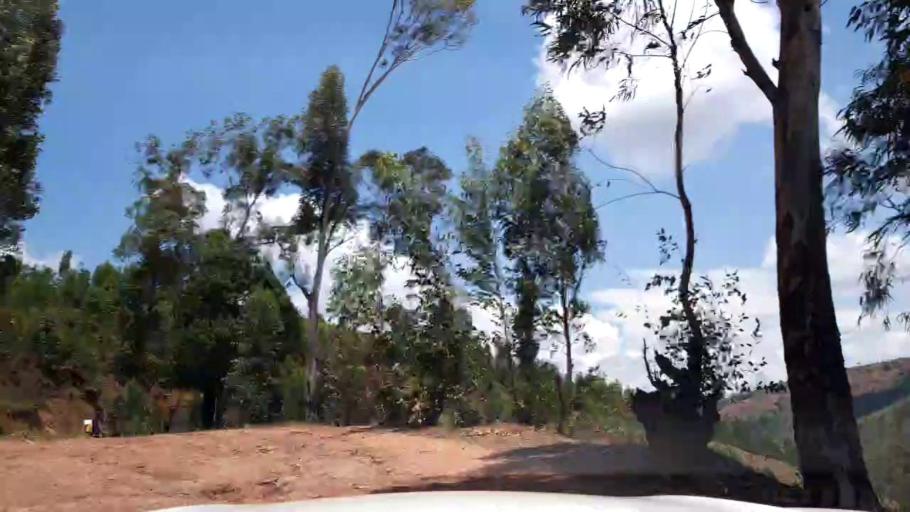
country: RW
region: Northern Province
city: Byumba
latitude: -1.5267
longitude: 30.1746
